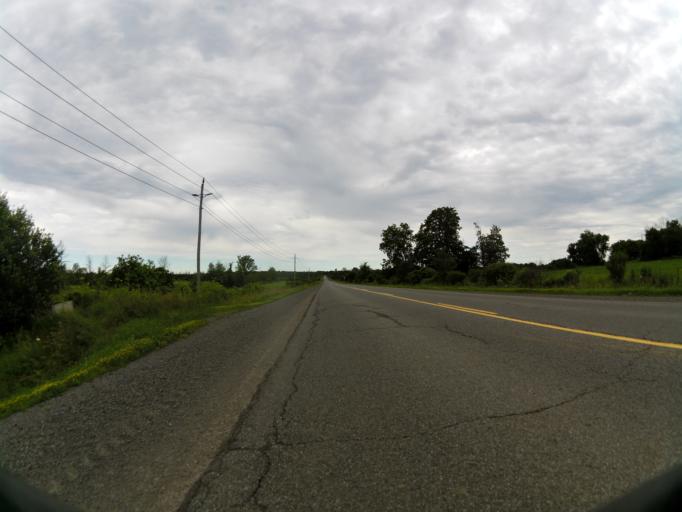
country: CA
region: Ontario
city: Ottawa
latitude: 45.2658
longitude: -75.6510
